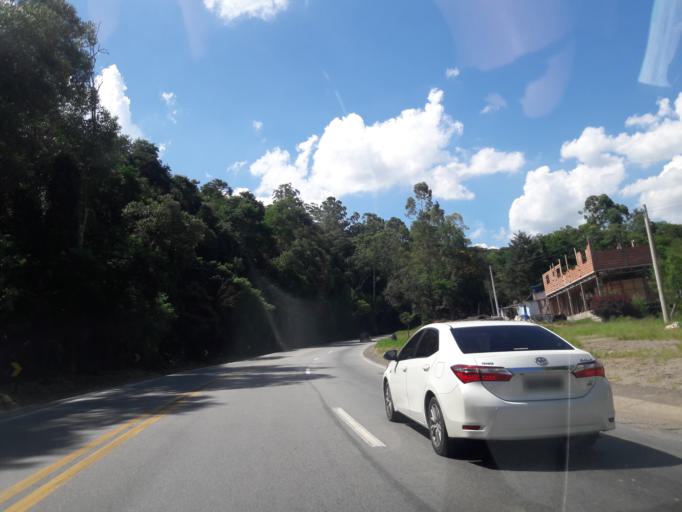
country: BR
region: Sao Paulo
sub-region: Francisco Morato
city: Francisco Morato
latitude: -23.2661
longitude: -46.7977
